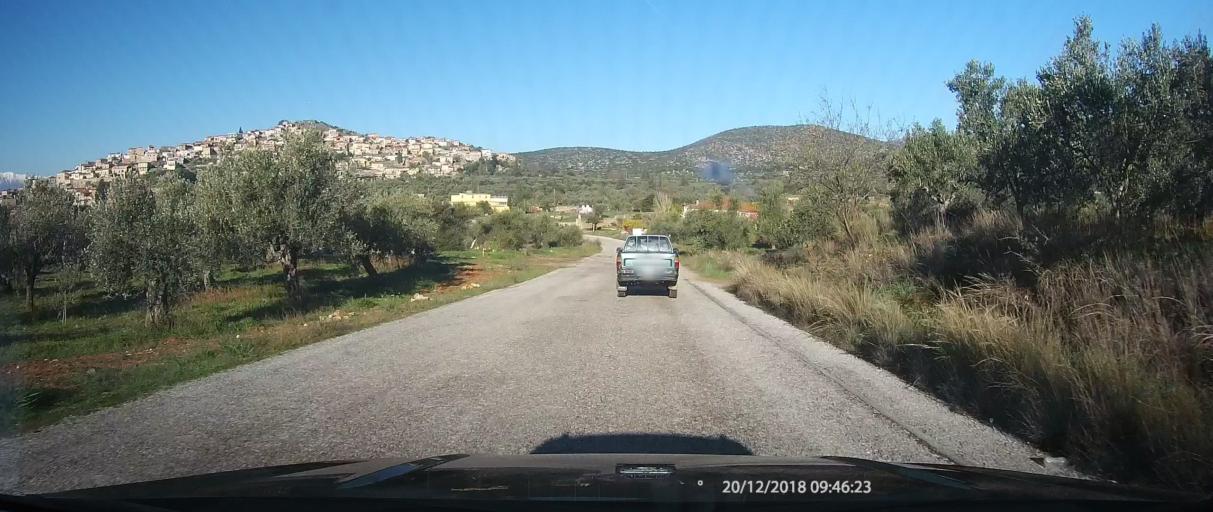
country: GR
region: Peloponnese
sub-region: Nomos Lakonias
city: Yerakion
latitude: 36.9911
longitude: 22.7150
